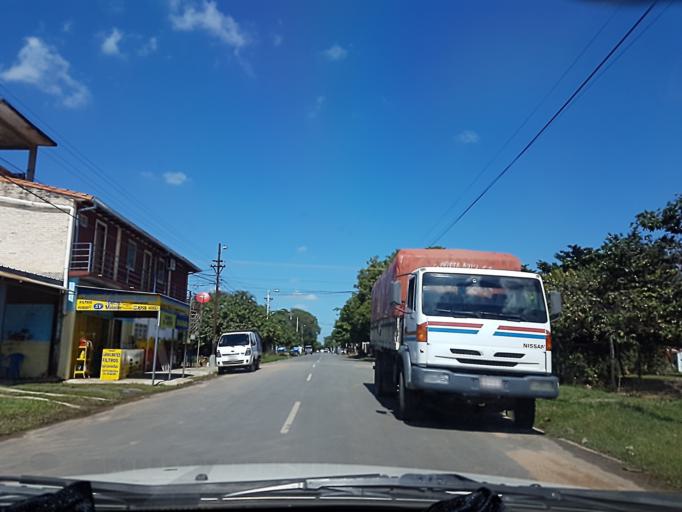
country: PY
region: Central
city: Colonia Mariano Roque Alonso
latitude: -25.2093
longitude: -57.5320
